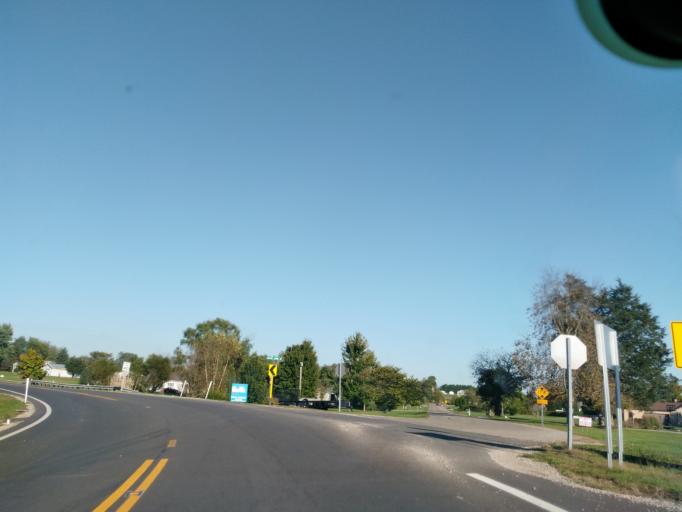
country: US
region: Ohio
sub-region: Ross County
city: Kingston
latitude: 39.4627
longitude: -82.9220
